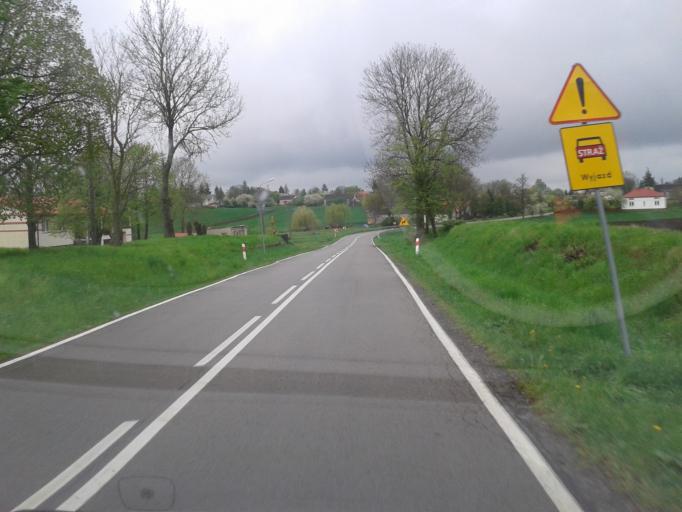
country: PL
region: Lublin Voivodeship
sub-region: Powiat hrubieszowski
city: Dolhobyczow
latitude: 50.5876
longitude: 23.9710
